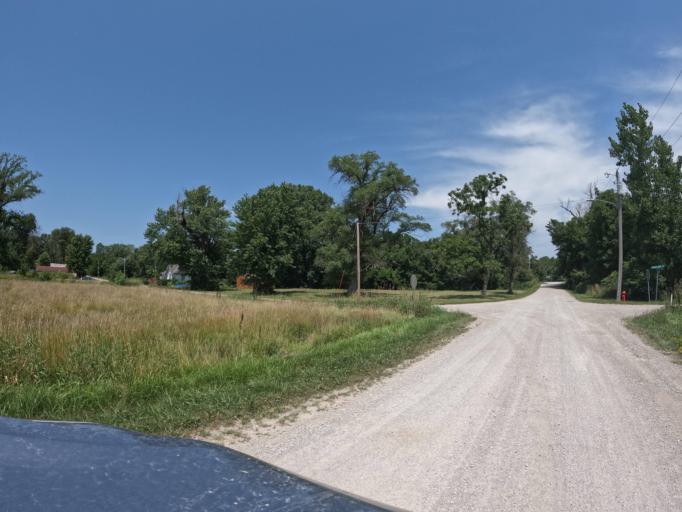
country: US
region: Iowa
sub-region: Appanoose County
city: Centerville
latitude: 40.7751
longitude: -92.9493
